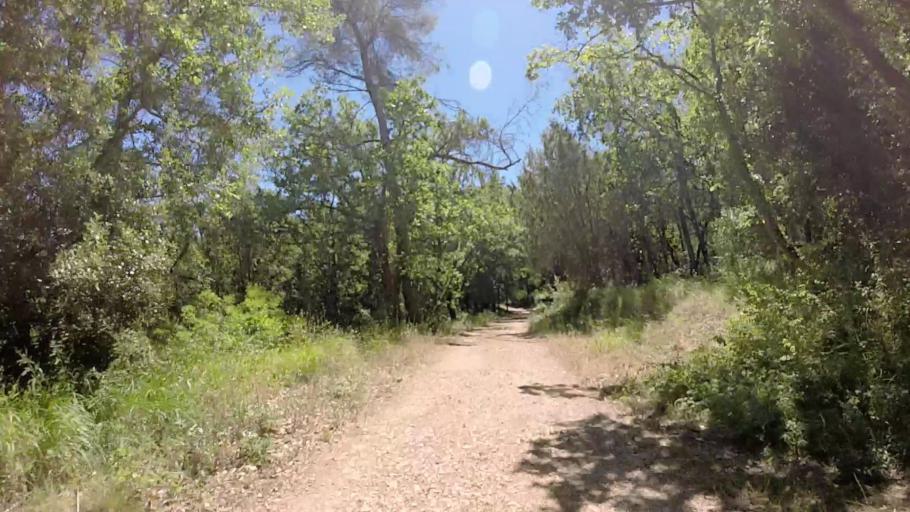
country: FR
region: Provence-Alpes-Cote d'Azur
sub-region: Departement des Alpes-Maritimes
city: Valbonne
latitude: 43.6355
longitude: 7.0276
